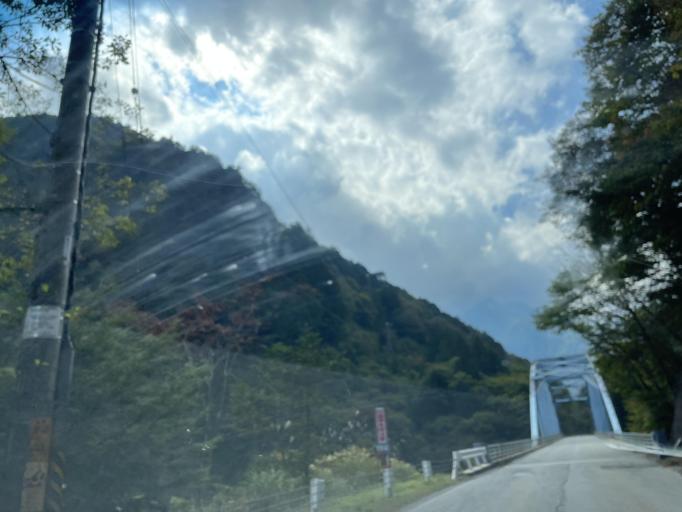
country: JP
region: Nagano
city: Omachi
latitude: 36.4987
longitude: 137.7579
